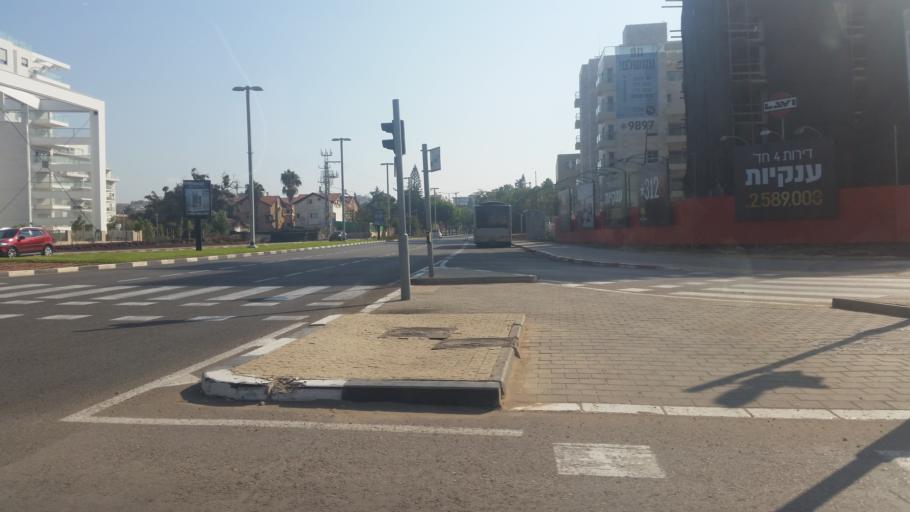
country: IL
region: Tel Aviv
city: Herzliyya
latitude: 32.1633
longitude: 34.8274
